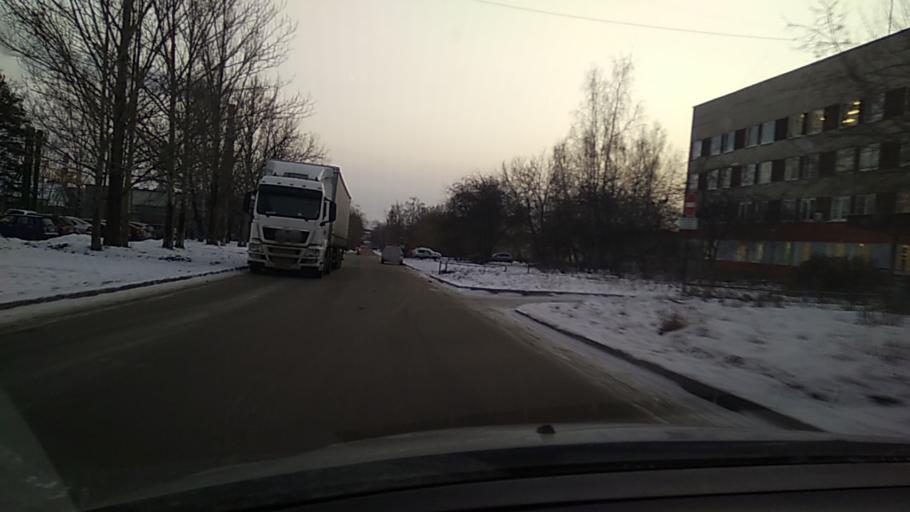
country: RU
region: Sverdlovsk
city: Istok
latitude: 56.7622
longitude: 60.7166
